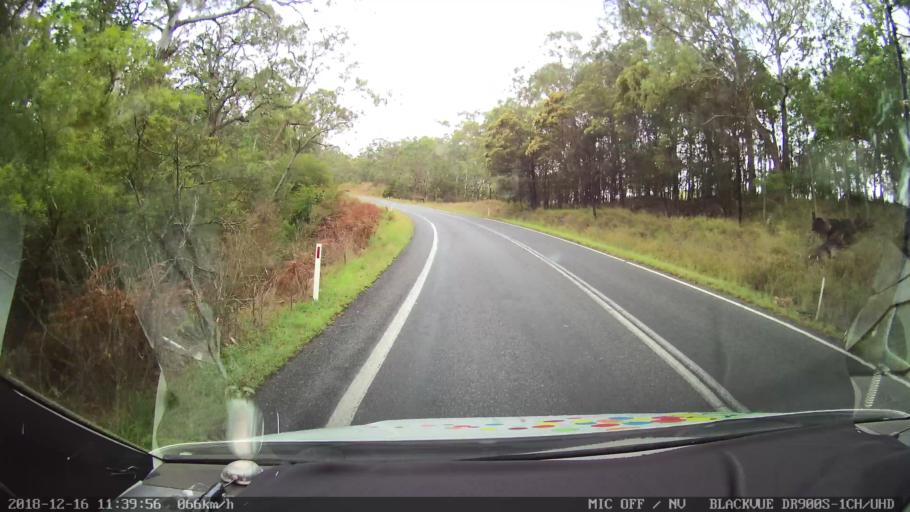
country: AU
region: New South Wales
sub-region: Tenterfield Municipality
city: Carrolls Creek
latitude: -28.9616
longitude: 152.1933
